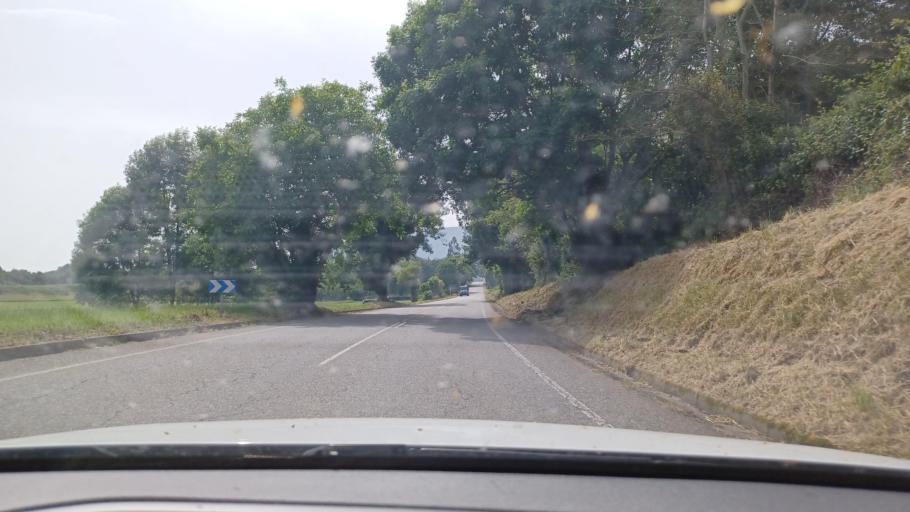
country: ES
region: Asturias
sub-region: Province of Asturias
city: Ribadesella
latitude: 43.4518
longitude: -5.0265
